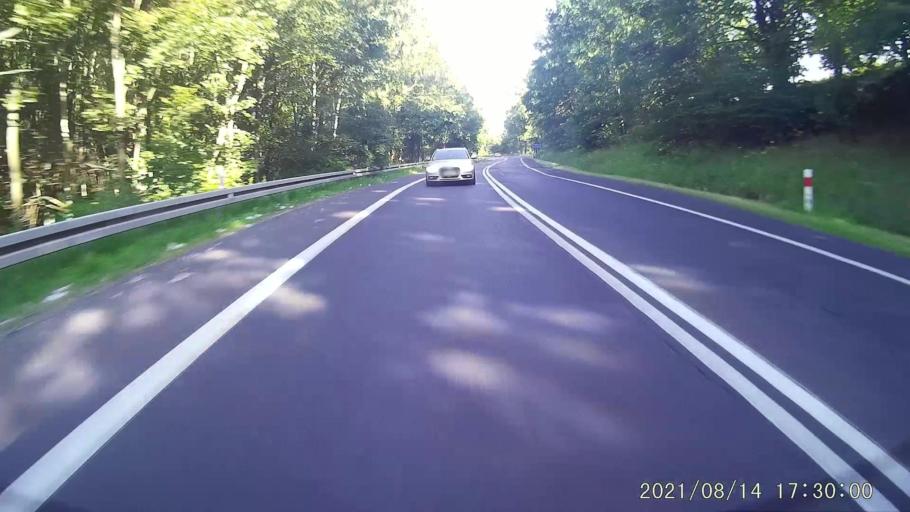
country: PL
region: Lower Silesian Voivodeship
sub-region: Jelenia Gora
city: Cieplice Slaskie Zdroj
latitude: 50.9113
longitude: 15.6611
